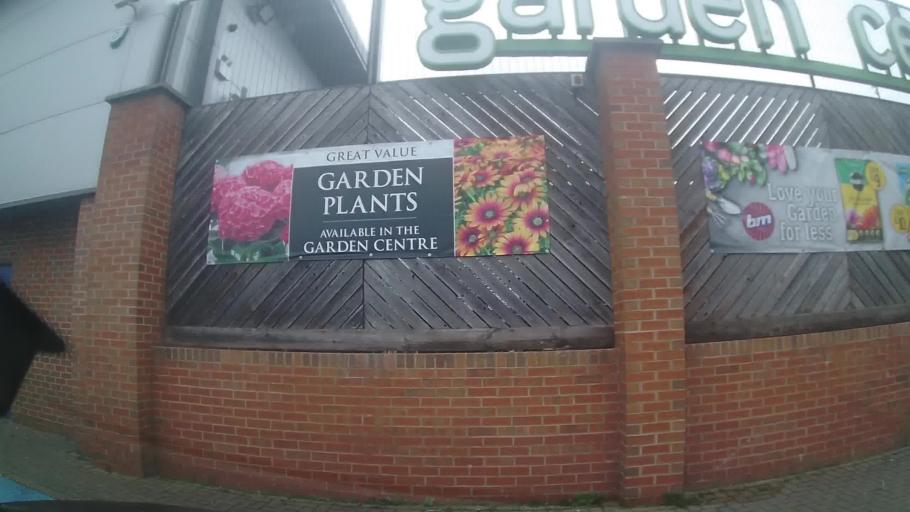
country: GB
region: England
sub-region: Shropshire
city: Whitchurch
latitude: 52.9668
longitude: -2.6698
